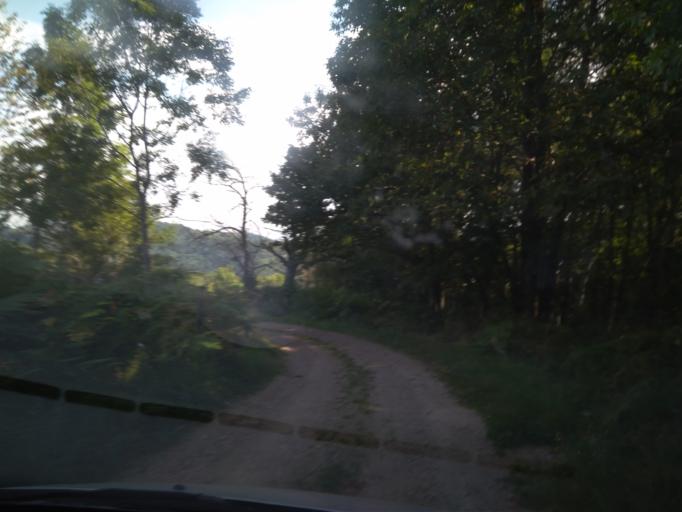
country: FR
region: Rhone-Alpes
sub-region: Departement de la Loire
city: La Pacaudiere
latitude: 46.1331
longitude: 3.7796
